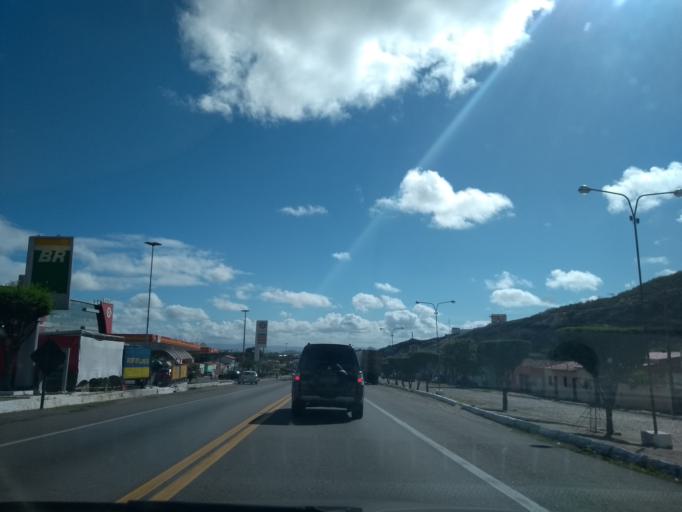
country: BR
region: Bahia
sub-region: Amargosa
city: Amargosa
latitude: -12.8723
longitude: -39.8565
